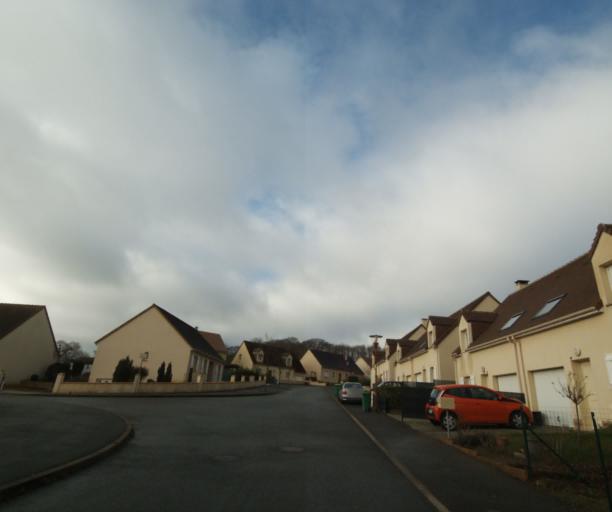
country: FR
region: Pays de la Loire
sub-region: Departement de la Sarthe
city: La Chapelle-Saint-Aubin
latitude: 48.0211
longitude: 0.1525
